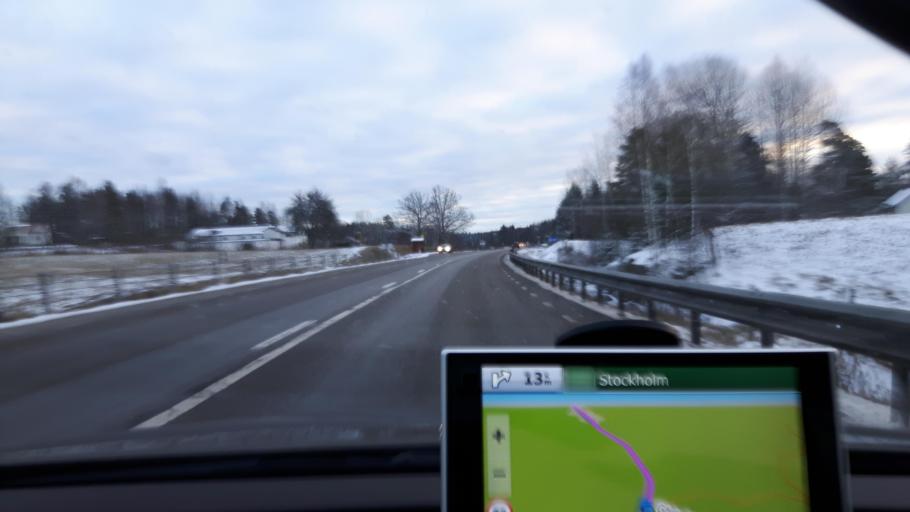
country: SE
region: Vaermland
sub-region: Saffle Kommun
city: Saeffle
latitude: 59.1535
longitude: 12.9742
